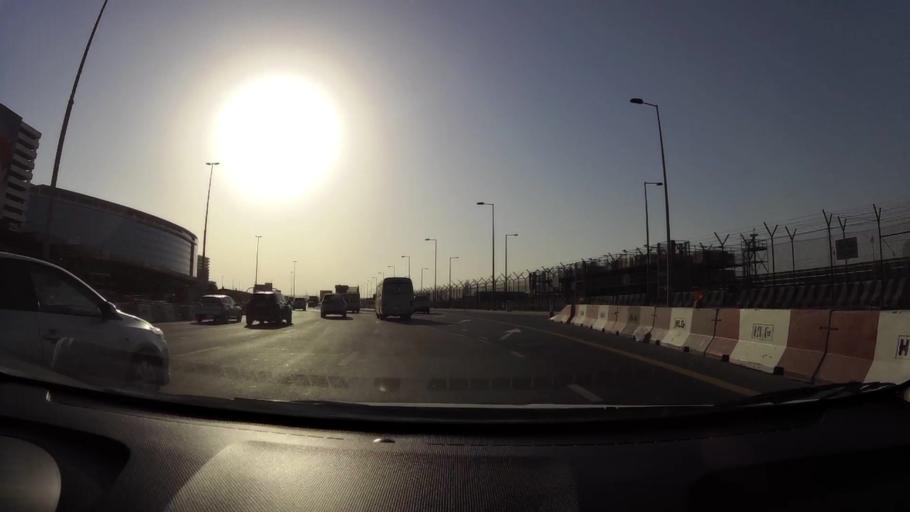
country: AE
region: Ash Shariqah
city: Sharjah
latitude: 25.2418
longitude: 55.3688
